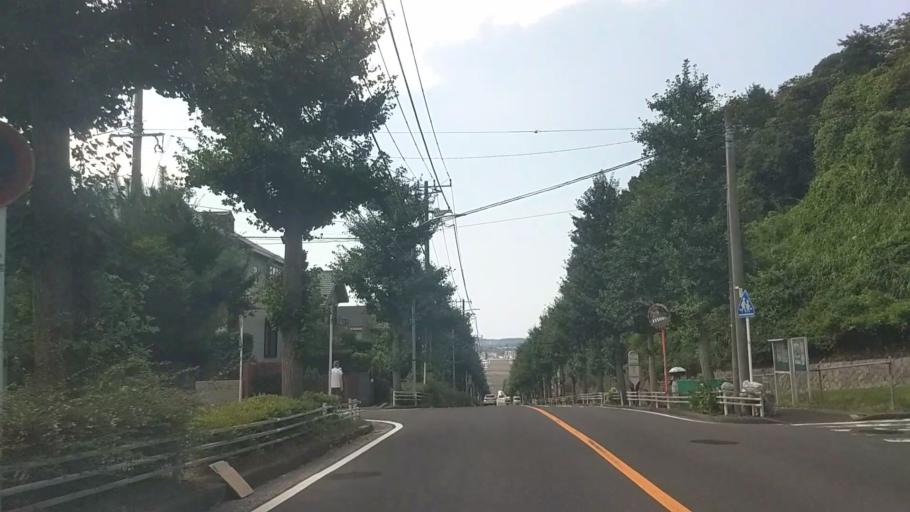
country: JP
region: Kanagawa
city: Yokosuka
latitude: 35.3449
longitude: 139.6331
